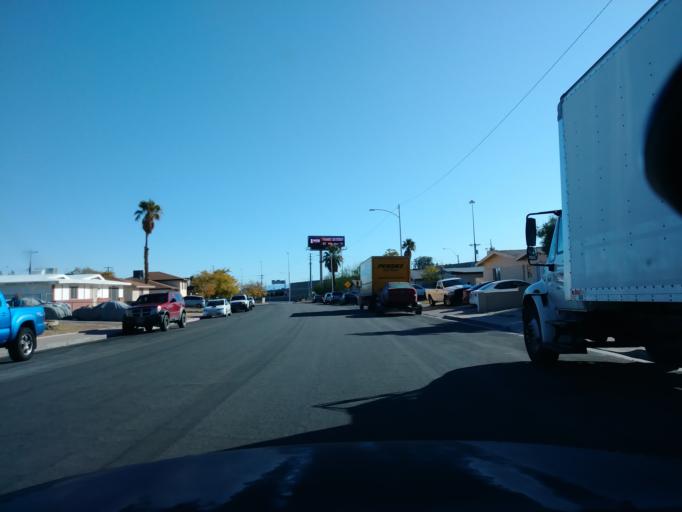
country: US
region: Nevada
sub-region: Clark County
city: Spring Valley
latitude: 36.1753
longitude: -115.2284
